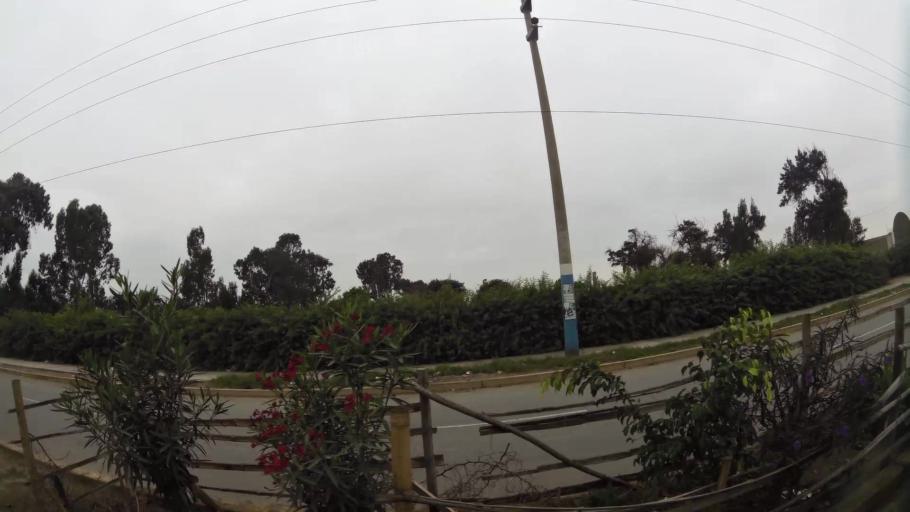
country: PE
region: Ica
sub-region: Provincia de Pisco
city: Pisco
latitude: -13.7259
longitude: -76.2033
